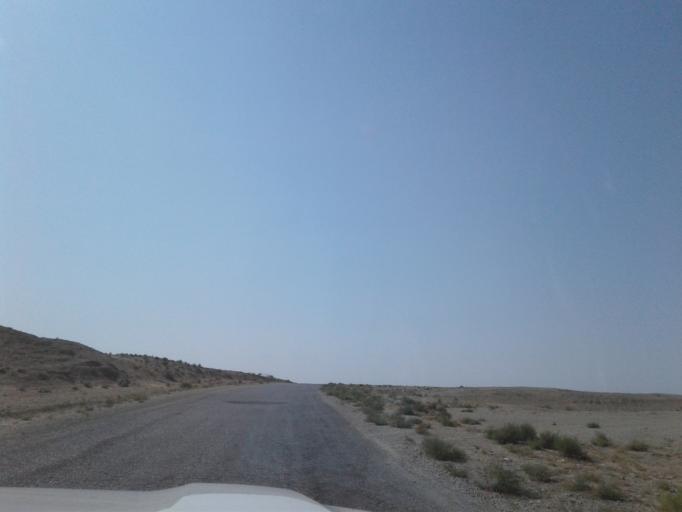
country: TM
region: Balkan
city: Gazanjyk
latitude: 39.2464
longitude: 55.3040
